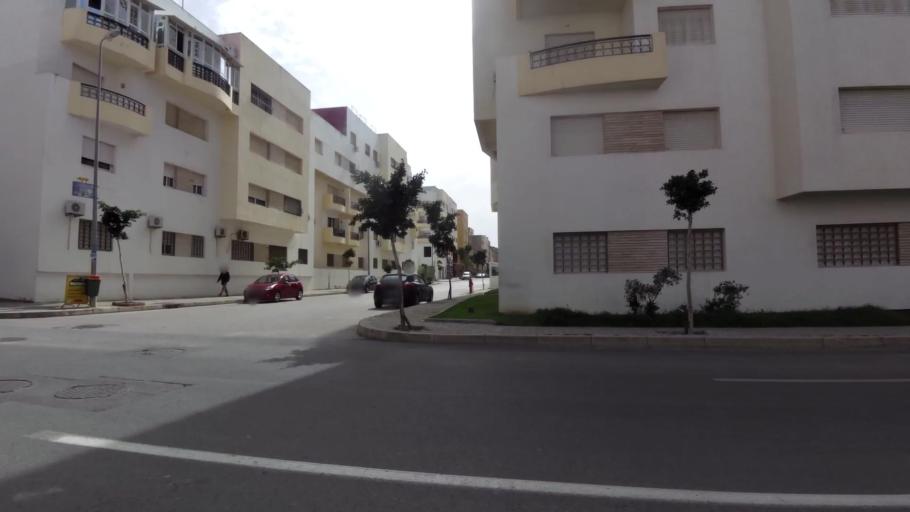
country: MA
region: Tanger-Tetouan
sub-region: Tanger-Assilah
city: Tangier
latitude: 35.7447
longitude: -5.8414
